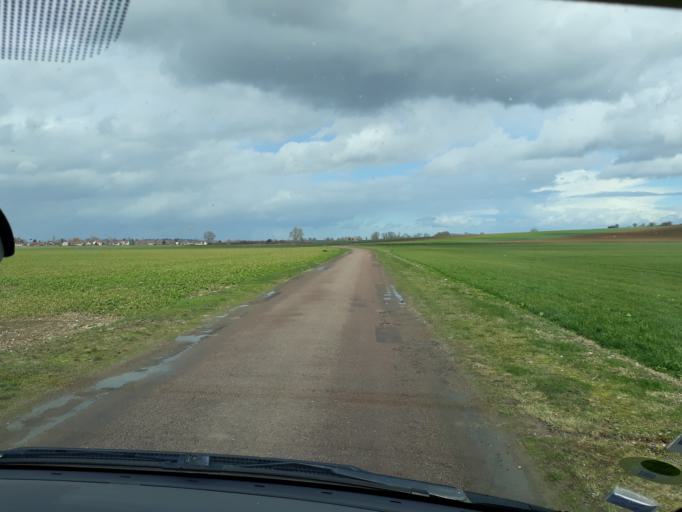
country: FR
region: Bourgogne
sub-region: Departement de la Cote-d'Or
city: Longecourt-en-Plaine
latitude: 47.2130
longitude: 5.1888
